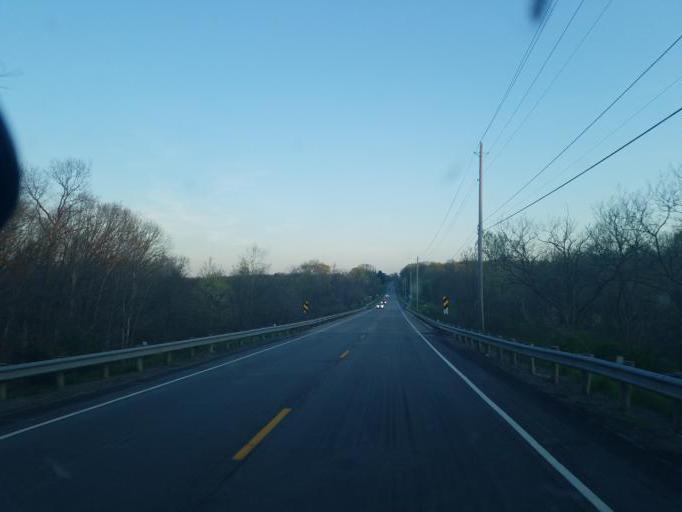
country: US
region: Ohio
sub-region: Trumbull County
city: Brookfield Center
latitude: 41.2739
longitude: -80.5685
